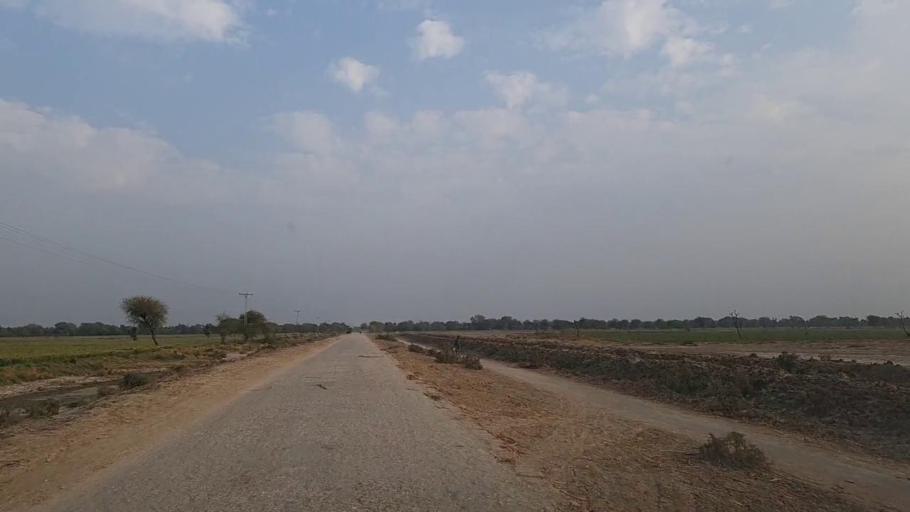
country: PK
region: Sindh
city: Mirwah Gorchani
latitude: 25.3034
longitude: 69.2169
